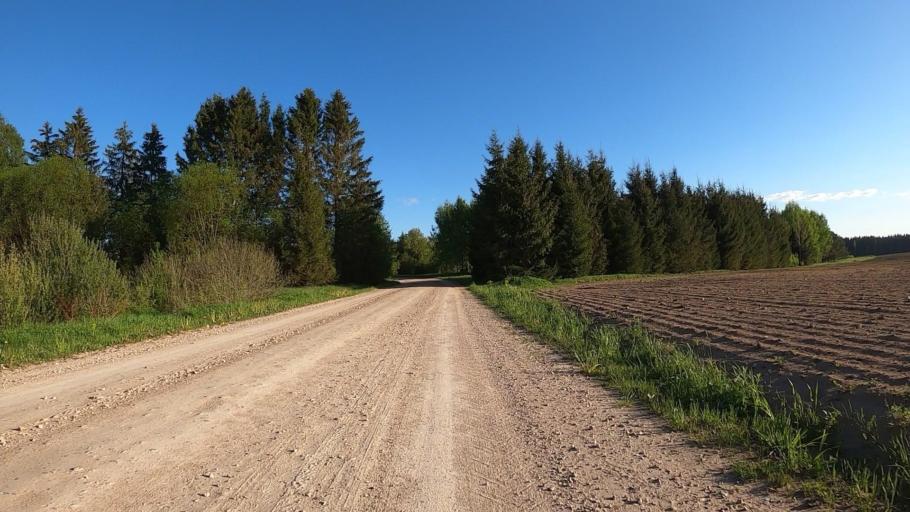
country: LV
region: Kekava
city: Kekava
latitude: 56.7684
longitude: 24.2873
